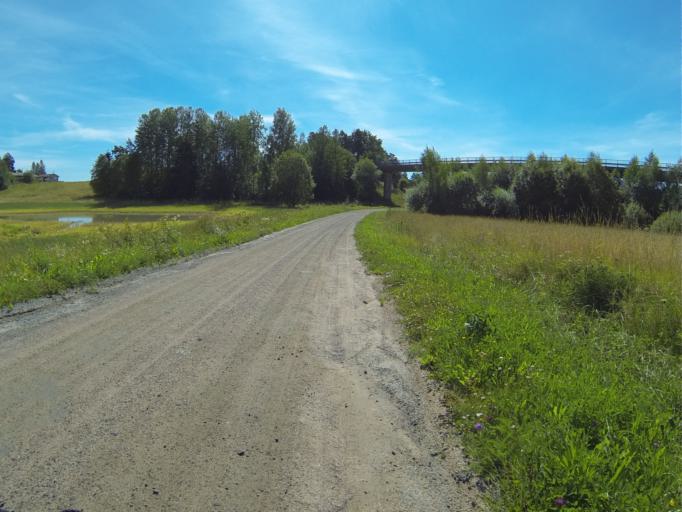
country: FI
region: Varsinais-Suomi
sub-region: Salo
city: Salo
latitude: 60.3062
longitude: 23.1084
